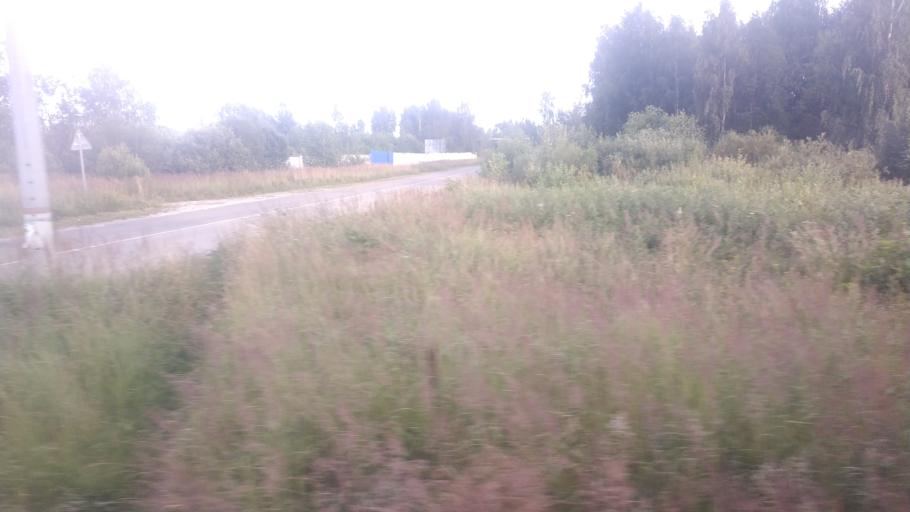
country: RU
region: Moskovskaya
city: Tugolesskiy Bor
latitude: 55.5528
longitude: 39.6958
